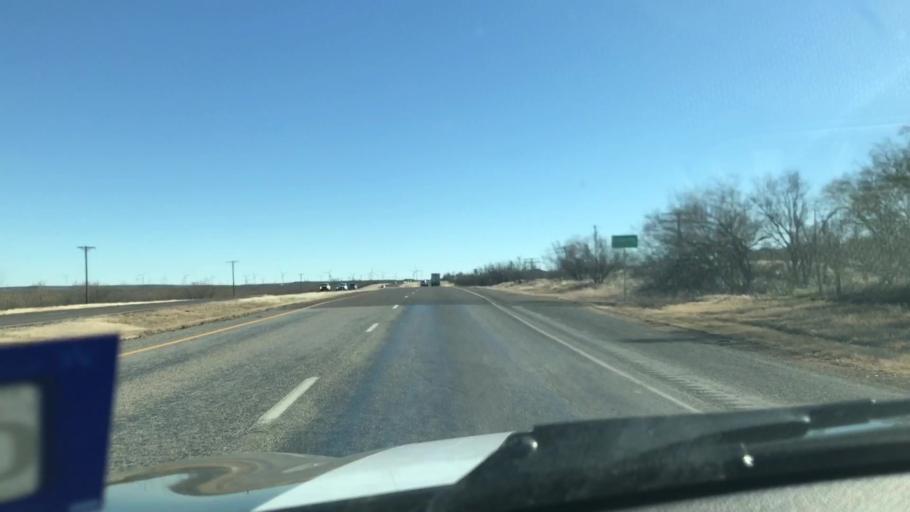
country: US
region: Texas
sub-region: Scurry County
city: Snyder
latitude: 32.9615
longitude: -101.0921
